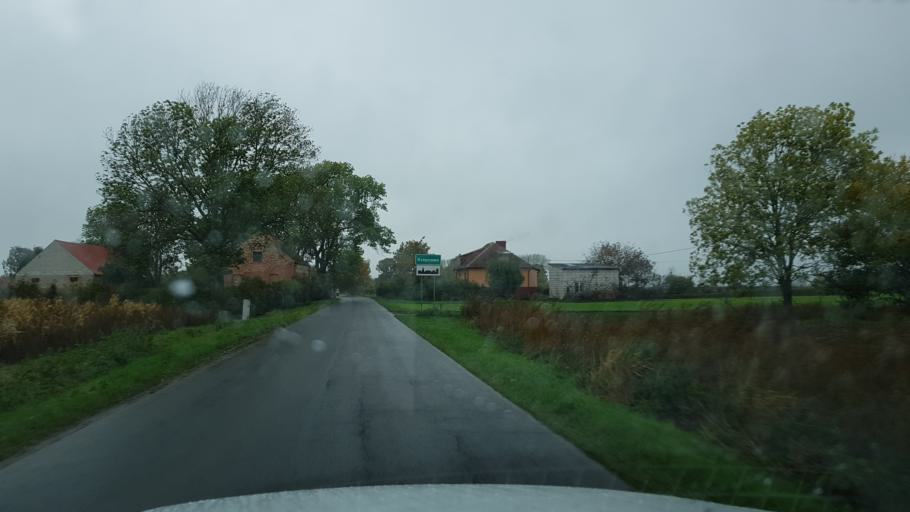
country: PL
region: West Pomeranian Voivodeship
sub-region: Powiat pyrzycki
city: Pyrzyce
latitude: 53.1590
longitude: 14.8502
